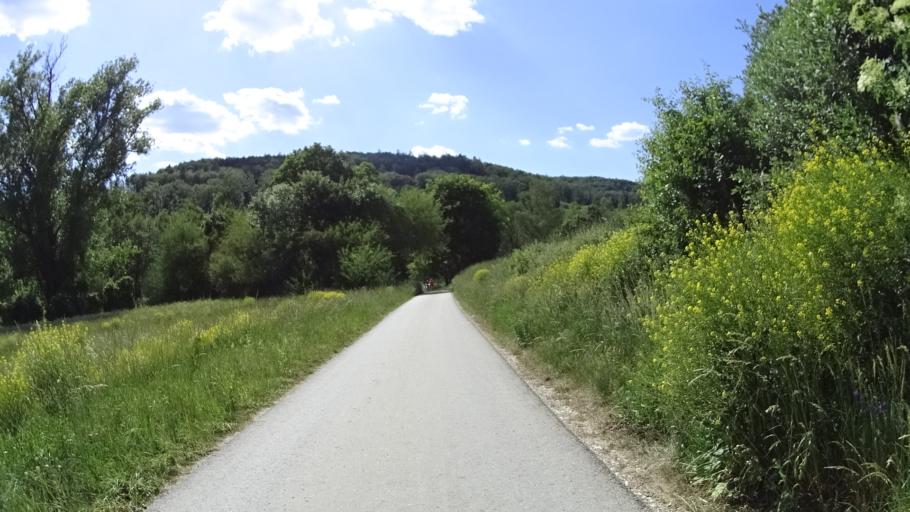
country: DE
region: Bavaria
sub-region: Regierungsbezirk Mittelfranken
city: Greding
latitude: 49.0176
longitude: 11.3584
